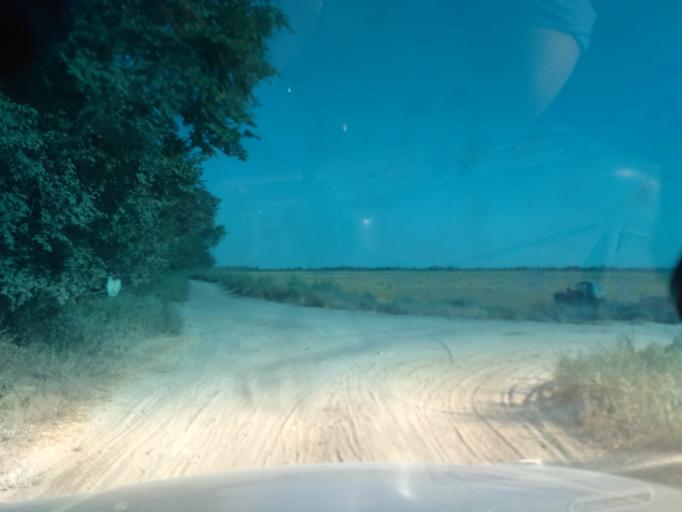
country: TJ
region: Viloyati Sughd
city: Buston
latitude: 40.5541
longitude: 69.0743
